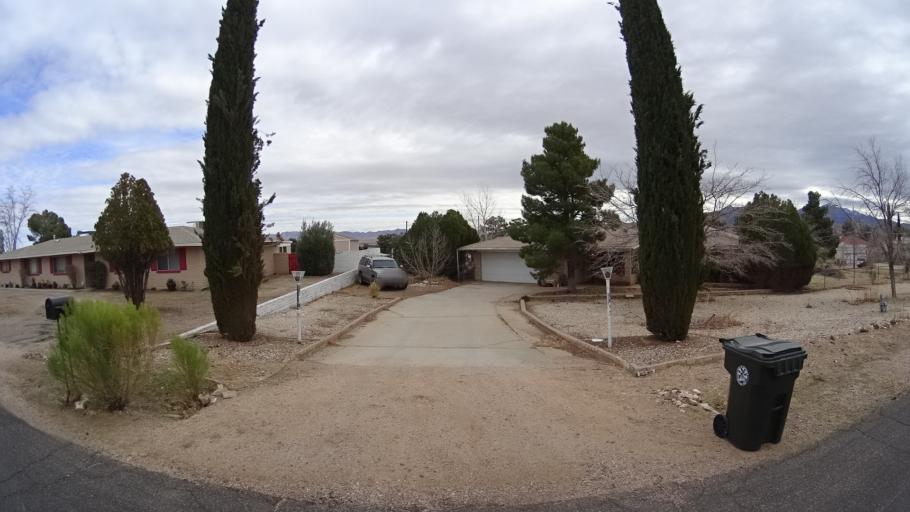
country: US
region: Arizona
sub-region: Mohave County
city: New Kingman-Butler
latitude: 35.2345
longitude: -114.0480
